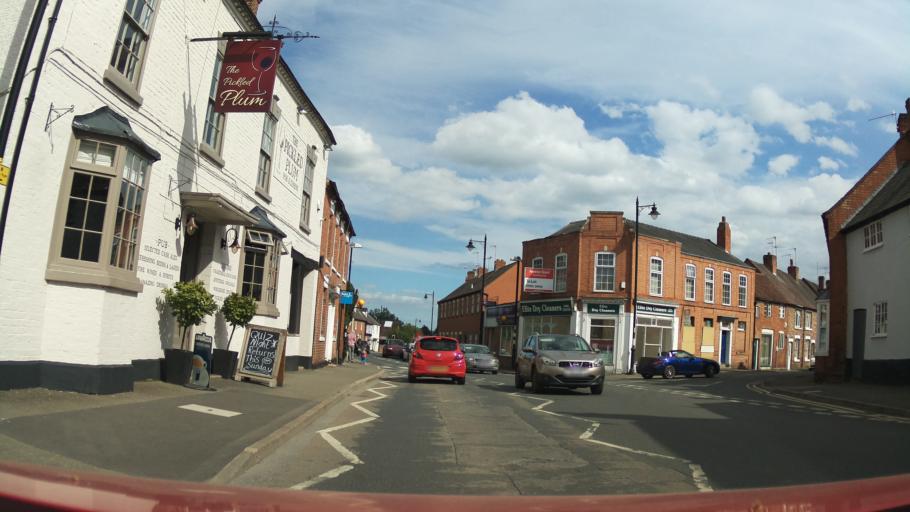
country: GB
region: England
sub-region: Worcestershire
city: Pershore
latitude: 52.1137
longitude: -2.0789
